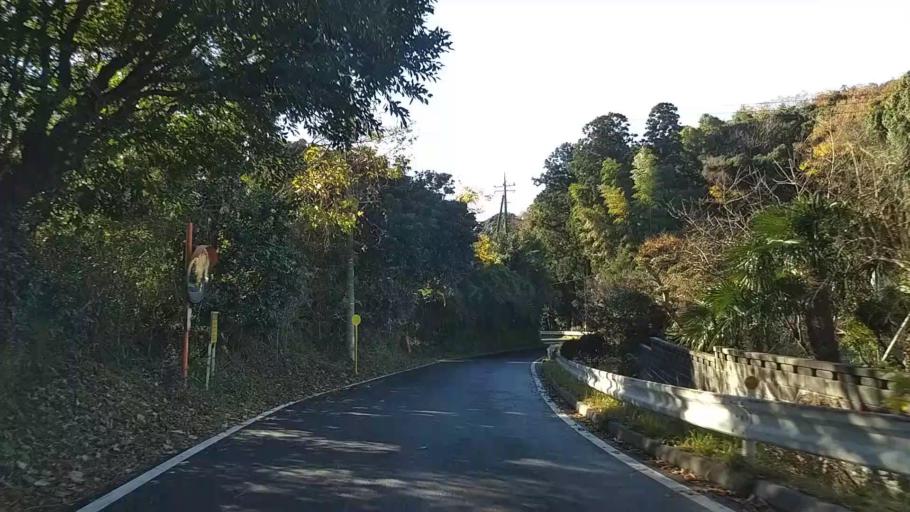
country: JP
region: Chiba
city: Futtsu
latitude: 35.2321
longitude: 139.8770
